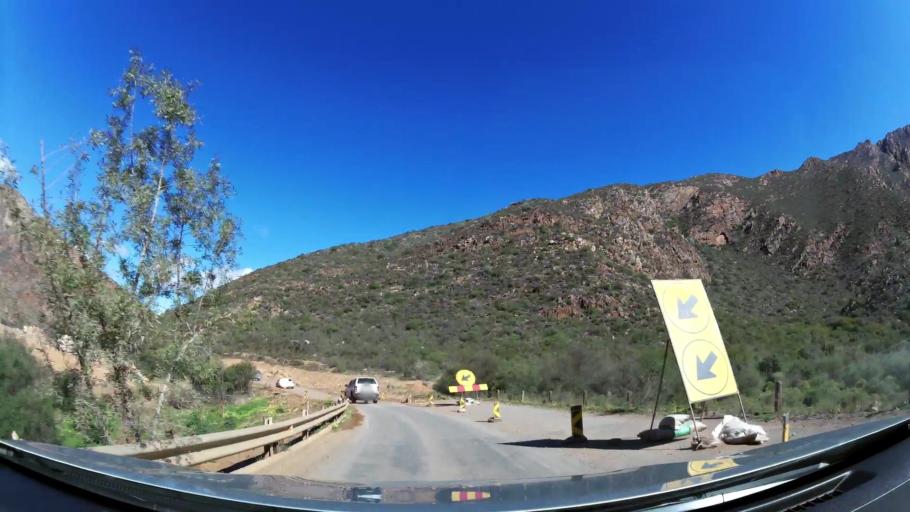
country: ZA
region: Western Cape
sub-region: Cape Winelands District Municipality
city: Ashton
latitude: -33.8037
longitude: 20.0939
